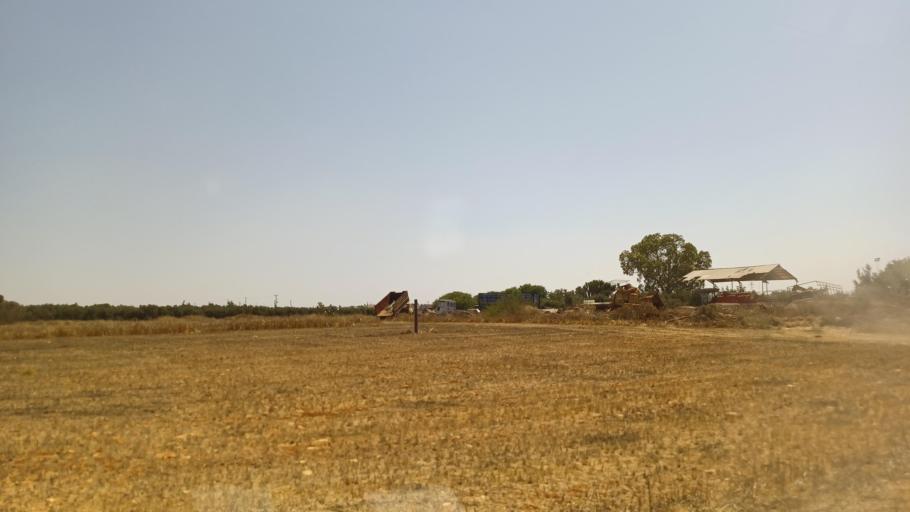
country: CY
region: Ammochostos
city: Avgorou
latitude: 35.0219
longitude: 33.8255
